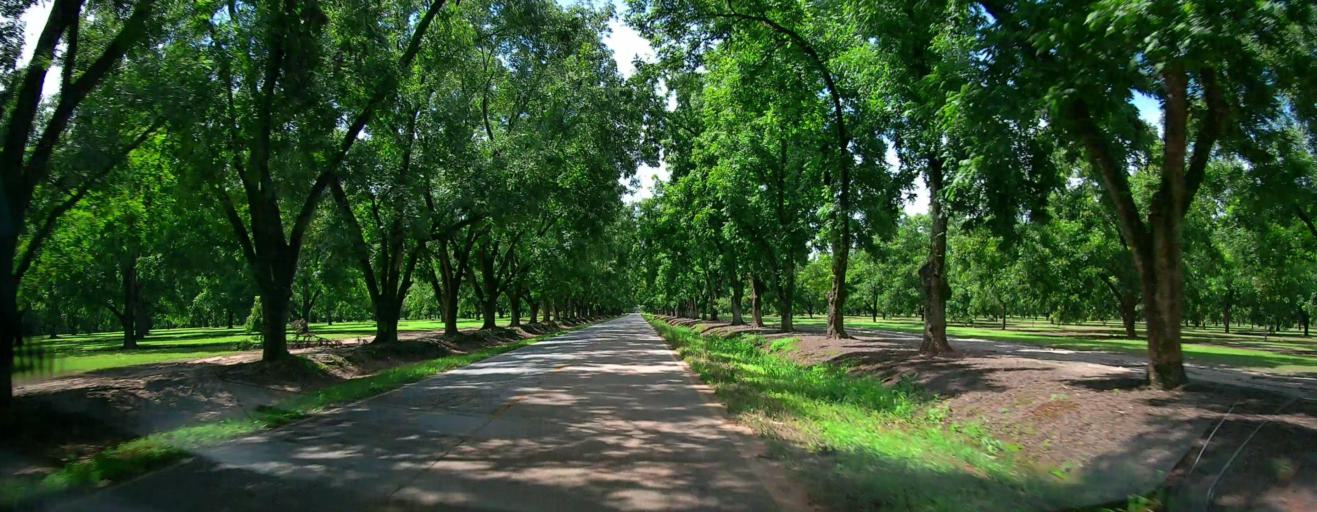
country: US
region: Georgia
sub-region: Houston County
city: Perry
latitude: 32.5212
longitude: -83.7873
